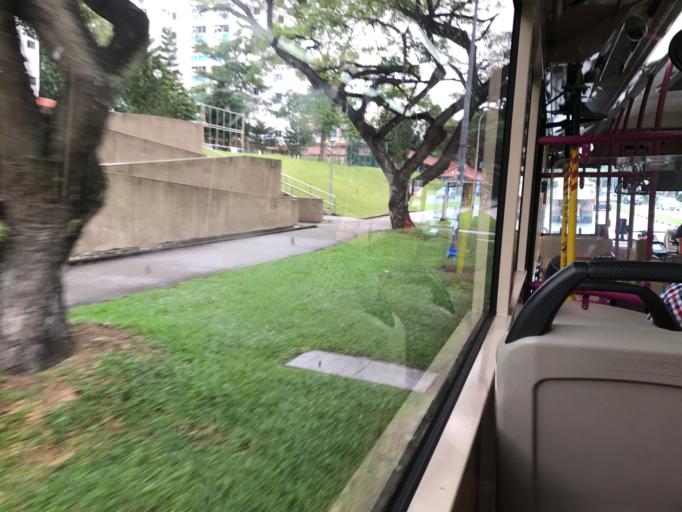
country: SG
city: Singapore
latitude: 1.3285
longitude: 103.9267
